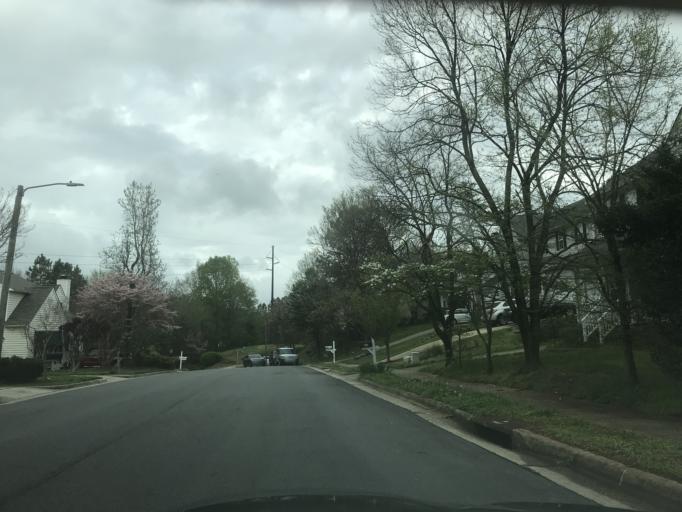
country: US
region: North Carolina
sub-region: Wake County
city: West Raleigh
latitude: 35.7487
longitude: -78.6854
